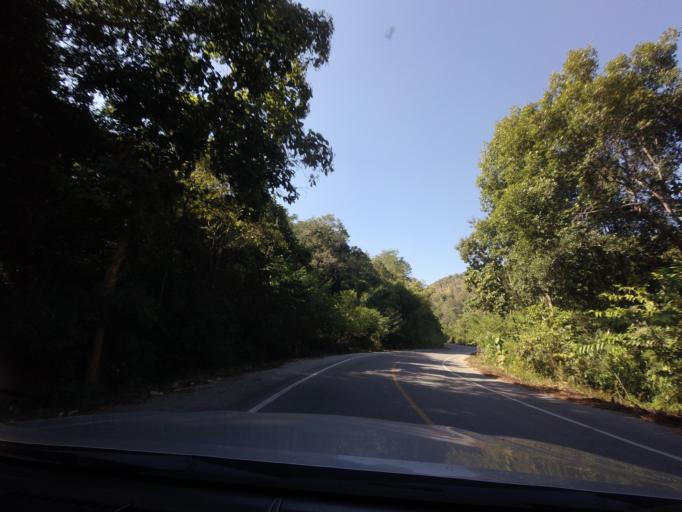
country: TH
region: Lampang
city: Chae Hom
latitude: 18.5504
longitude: 99.6320
